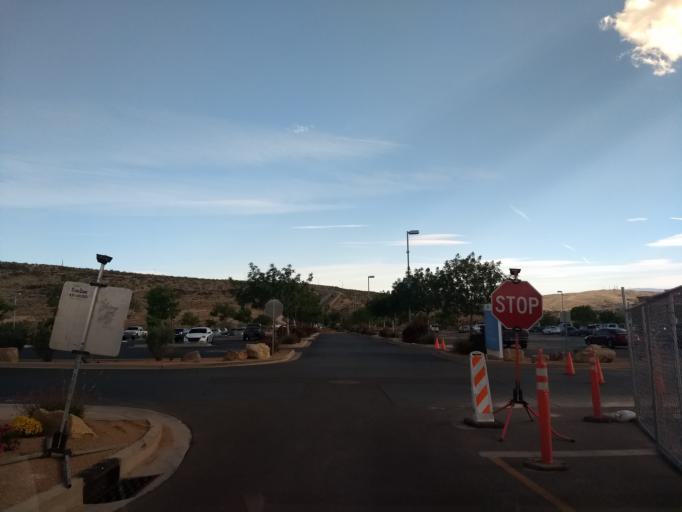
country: US
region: Utah
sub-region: Washington County
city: Saint George
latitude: 37.0976
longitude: -113.5504
